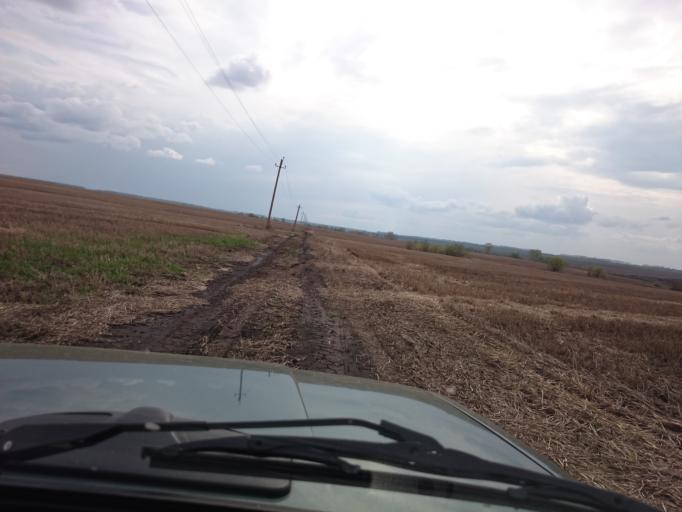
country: RU
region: Mordoviya
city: Kadoshkino
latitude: 54.0215
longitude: 44.4710
